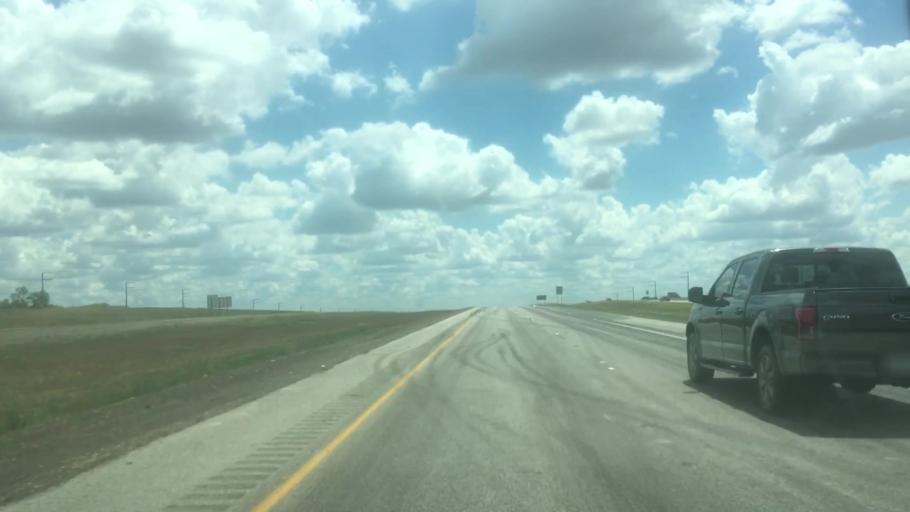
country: US
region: Texas
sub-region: Caldwell County
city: Lockhart
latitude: 29.9838
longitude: -97.6821
